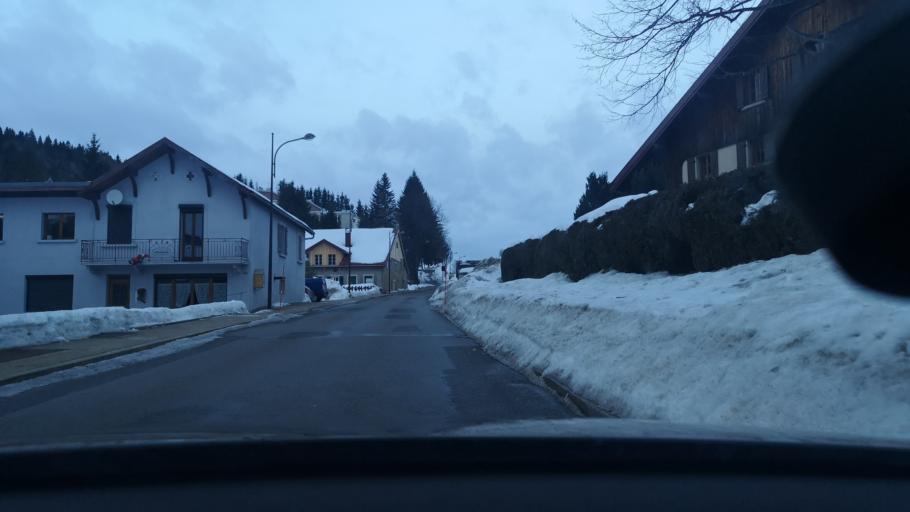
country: FR
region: Franche-Comte
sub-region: Departement du Doubs
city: Jougne
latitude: 46.7787
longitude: 6.3727
